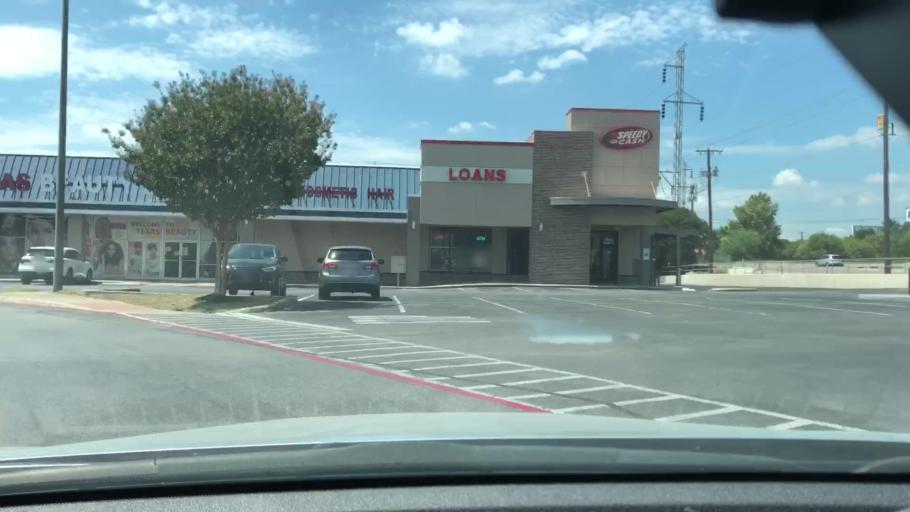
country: US
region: Texas
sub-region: Bexar County
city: Terrell Hills
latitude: 29.4939
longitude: -98.4320
